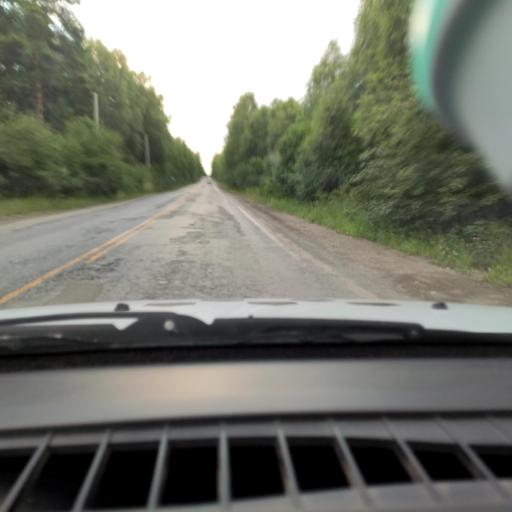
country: RU
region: Chelyabinsk
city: Karabash
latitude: 55.5323
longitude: 60.3426
